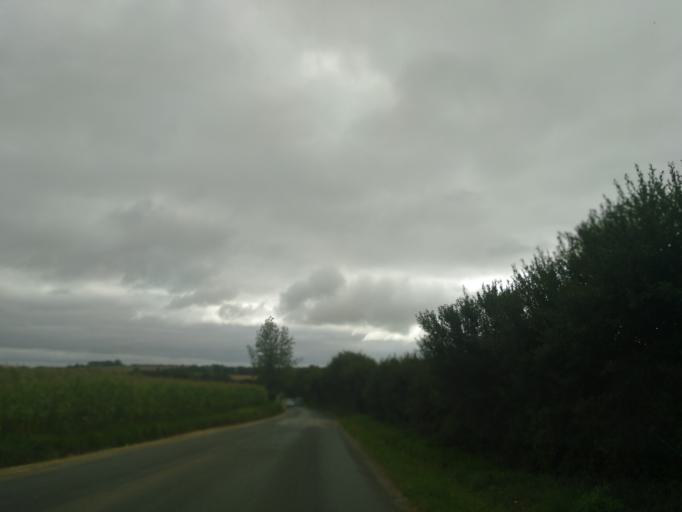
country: FR
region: Brittany
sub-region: Departement du Finistere
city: Plomodiern
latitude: 48.1562
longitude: -4.2449
